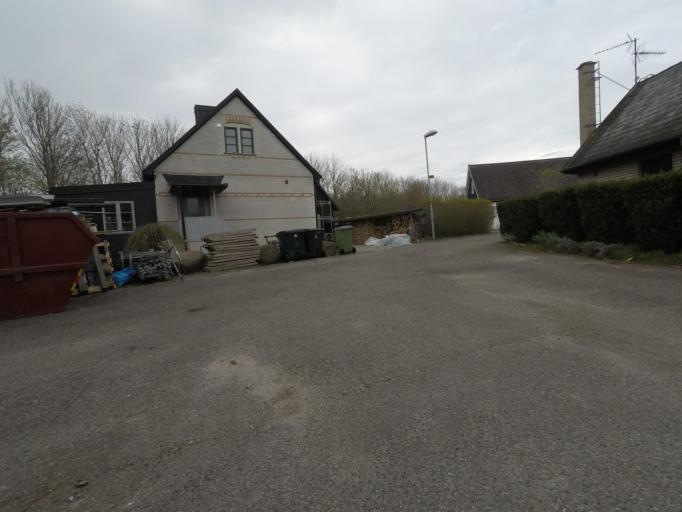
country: SE
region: Skane
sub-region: Lomma Kommun
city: Lomma
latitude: 55.6629
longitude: 13.0644
